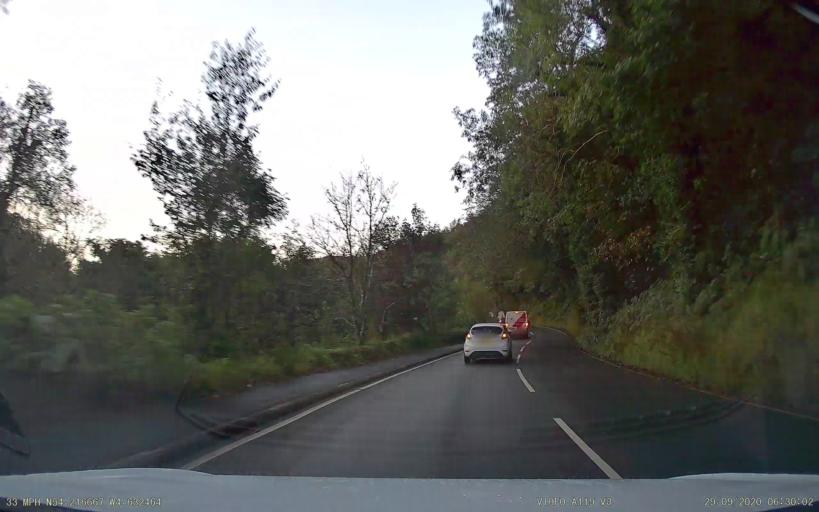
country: IM
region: Castletown
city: Castletown
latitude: 54.2167
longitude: -4.6325
